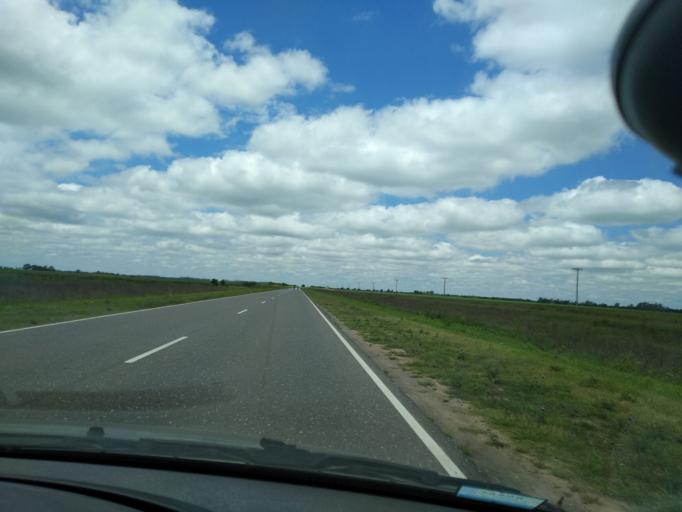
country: AR
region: Cordoba
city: Toledo
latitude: -31.6452
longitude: -64.0139
